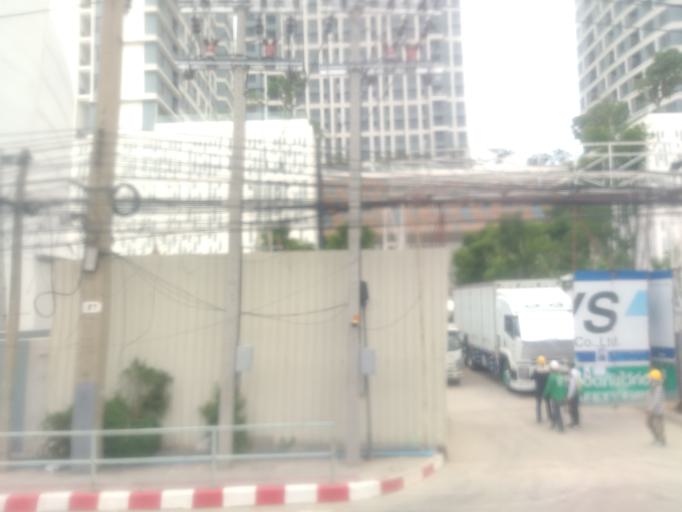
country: TH
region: Bangkok
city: Chatuchak
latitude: 13.8114
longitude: 100.5599
